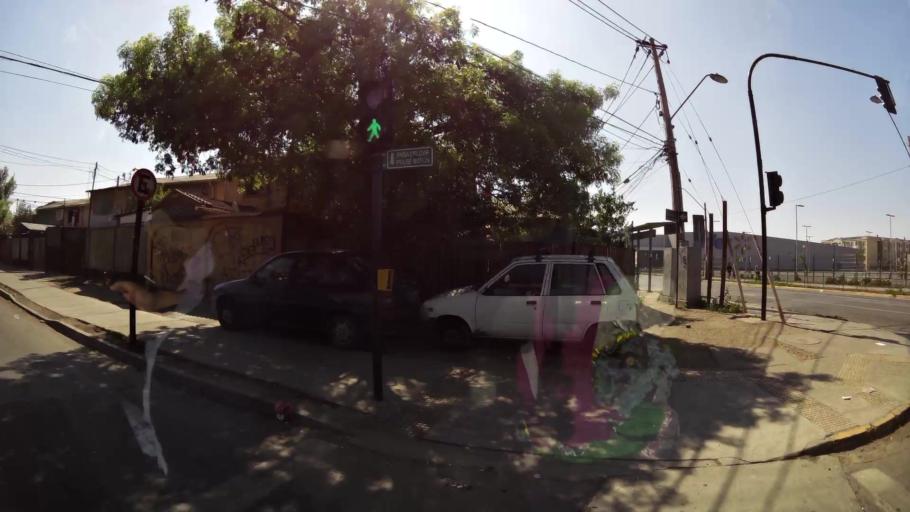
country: CL
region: Santiago Metropolitan
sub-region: Provincia de Santiago
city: Lo Prado
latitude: -33.3604
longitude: -70.7465
